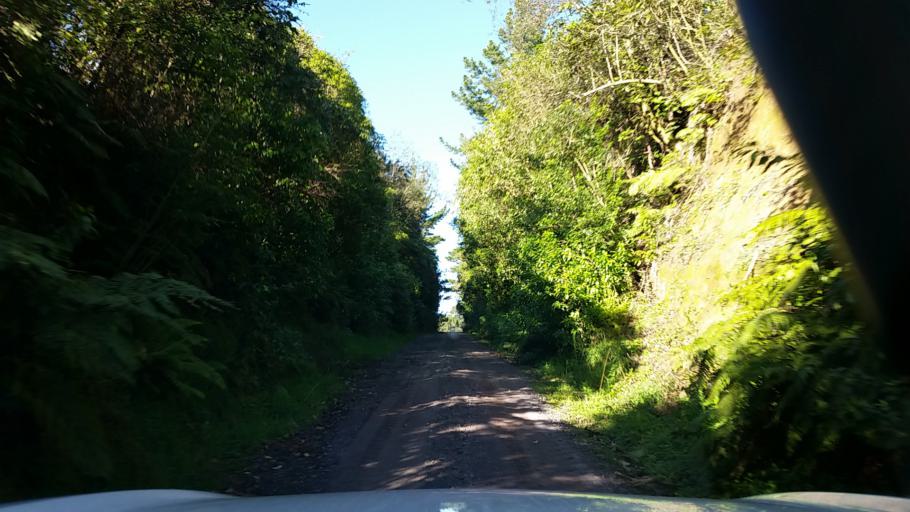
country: NZ
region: Waikato
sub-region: Taupo District
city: Taupo
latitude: -38.4081
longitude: 176.1404
